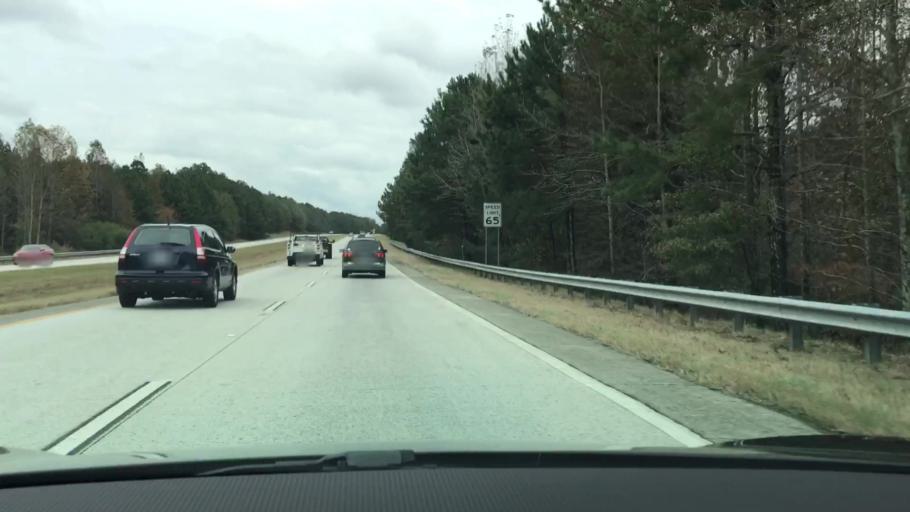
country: US
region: Georgia
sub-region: Barrow County
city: Statham
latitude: 33.9541
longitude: -83.5997
